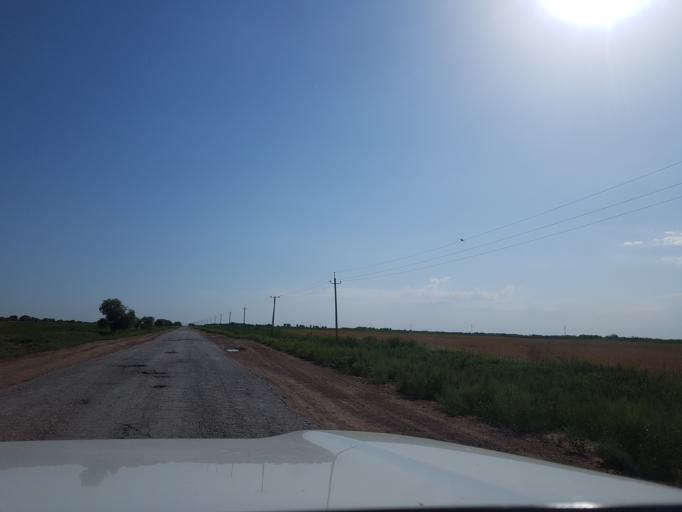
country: TM
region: Dasoguz
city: Koeneuergench
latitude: 42.0365
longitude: 58.8101
